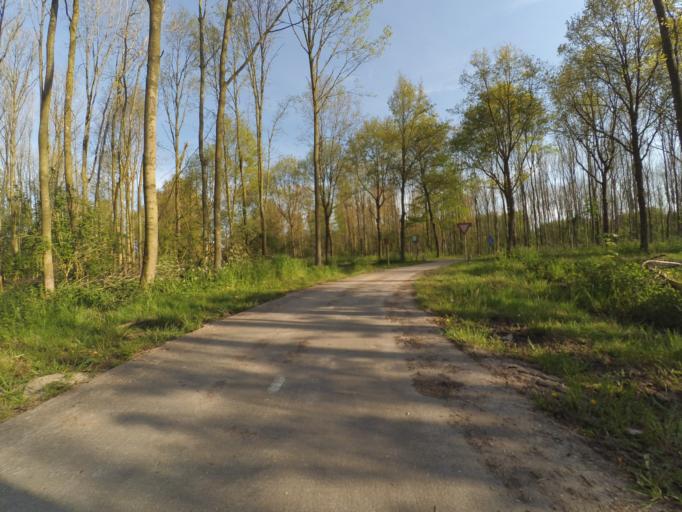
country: NL
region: North Holland
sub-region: Gemeente Huizen
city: Huizen
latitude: 52.3481
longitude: 5.2828
